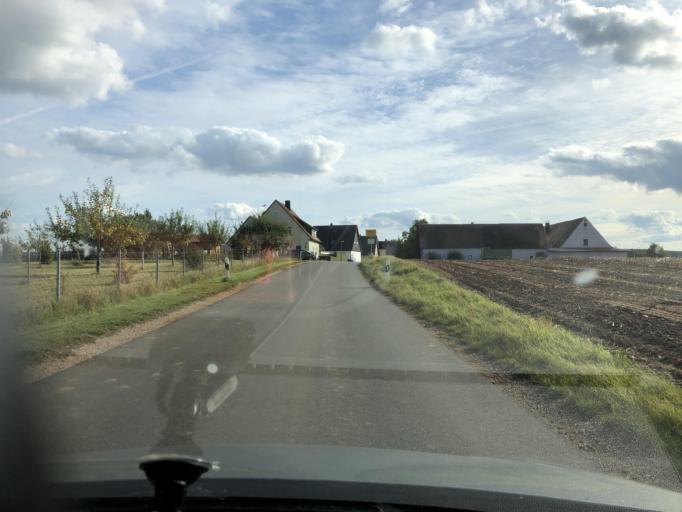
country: DE
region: Bavaria
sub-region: Regierungsbezirk Mittelfranken
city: Cadolzburg
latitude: 49.4760
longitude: 10.8250
